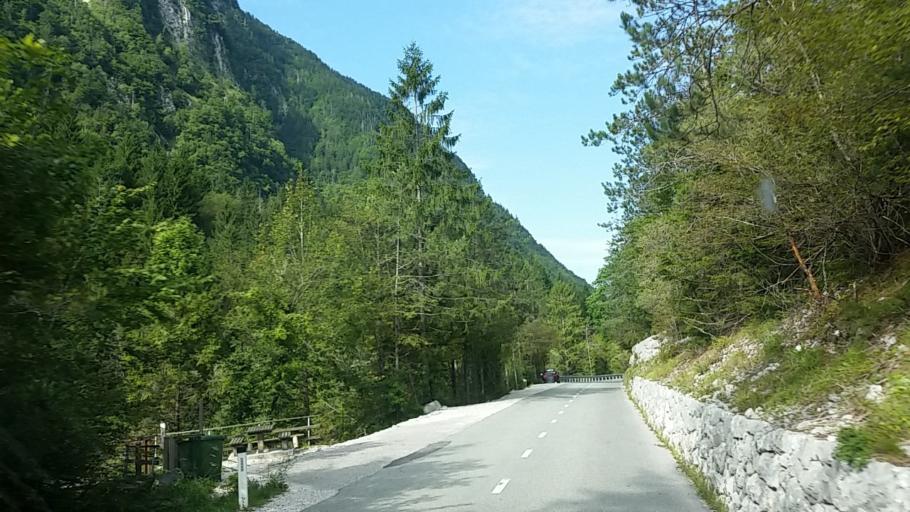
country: SI
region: Bovec
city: Bovec
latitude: 46.3375
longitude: 13.6225
